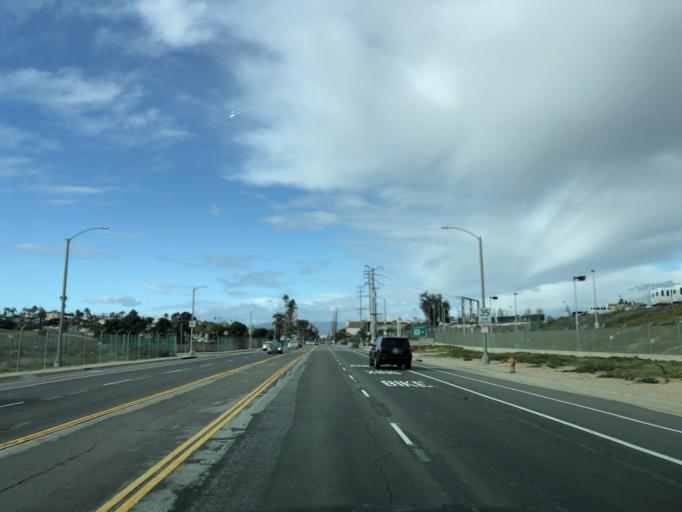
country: US
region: California
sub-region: Los Angeles County
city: Marina del Rey
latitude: 33.9496
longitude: -118.4379
